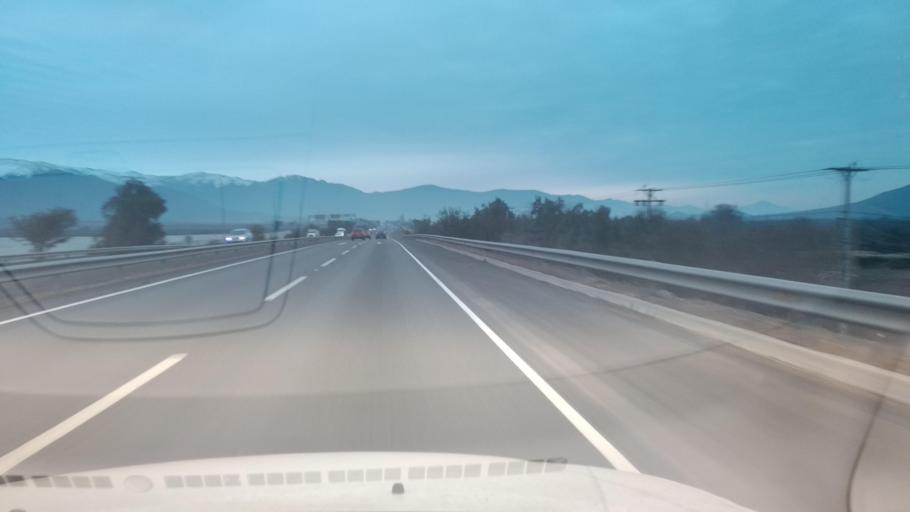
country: CL
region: Santiago Metropolitan
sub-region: Provincia de Chacabuco
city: Chicureo Abajo
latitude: -33.1460
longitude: -70.6583
